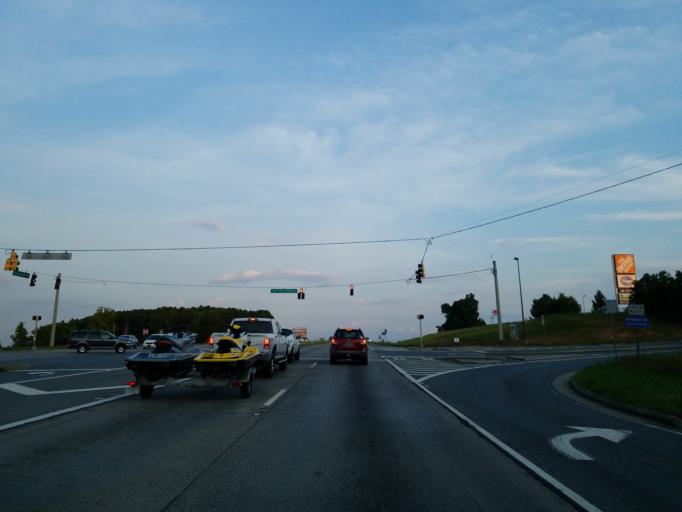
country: US
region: Georgia
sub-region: Pickens County
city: Jasper
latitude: 34.4700
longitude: -84.4613
